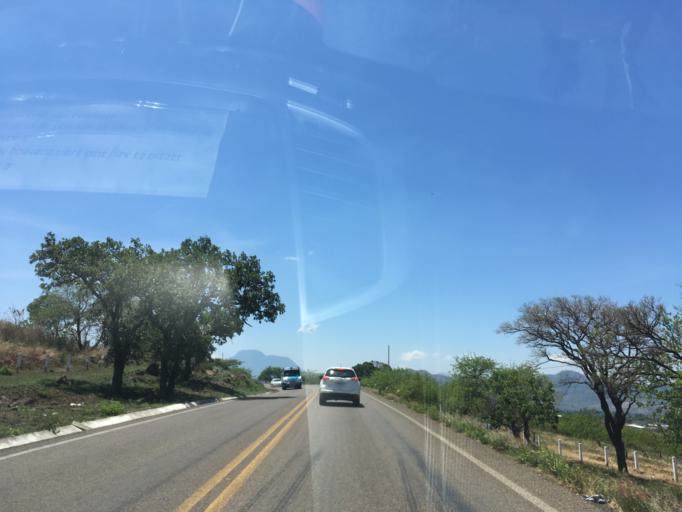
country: MX
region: Michoacan
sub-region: Tuxpan
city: La Soledad
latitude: 19.4958
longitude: -100.4583
